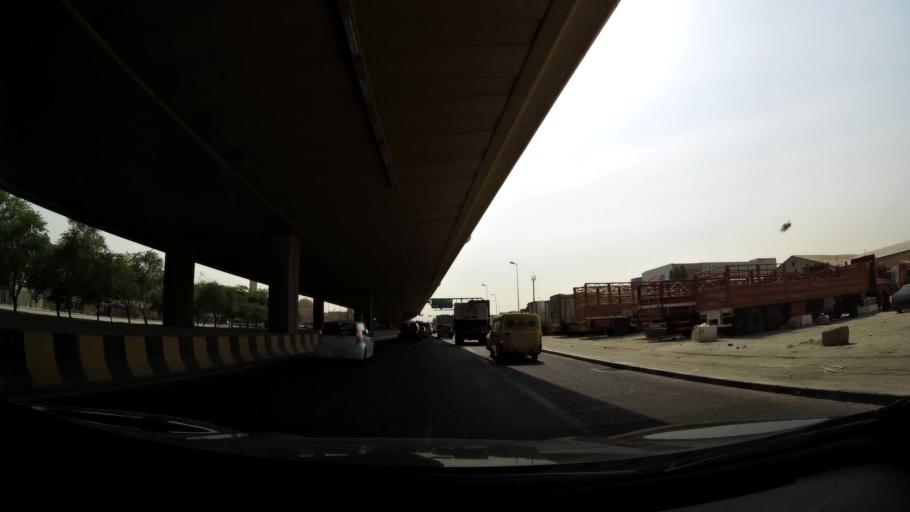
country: KW
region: Al Asimah
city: Ar Rabiyah
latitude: 29.3252
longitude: 47.9349
